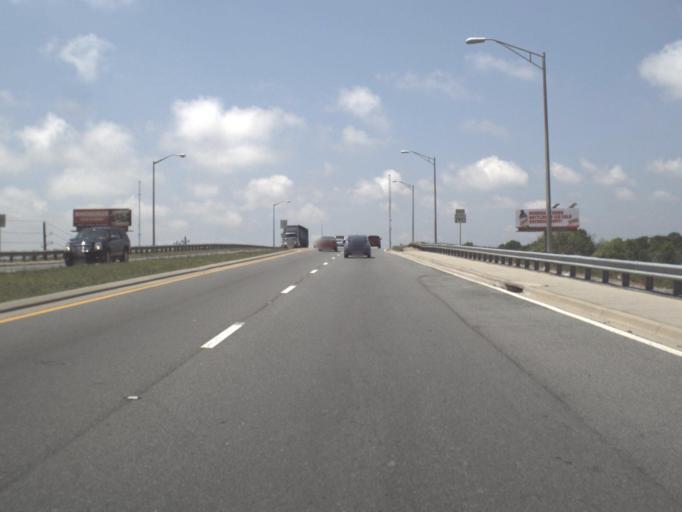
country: US
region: Florida
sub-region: Escambia County
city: Goulding
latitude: 30.4502
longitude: -87.2245
